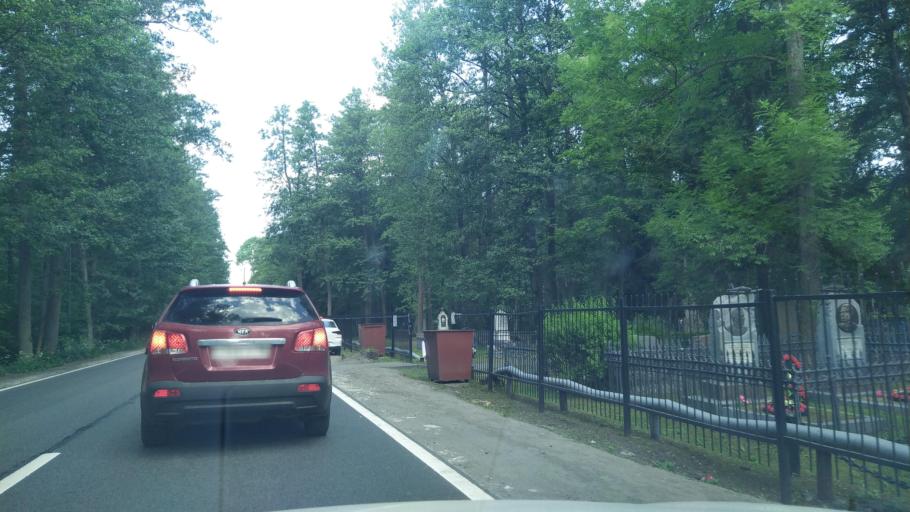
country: RU
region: St.-Petersburg
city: Kronshtadt
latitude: 60.0168
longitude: 29.7084
